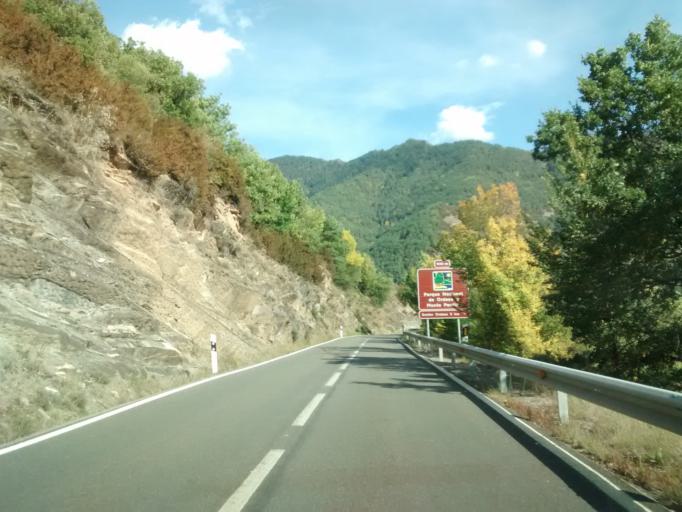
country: ES
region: Aragon
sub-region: Provincia de Huesca
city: Broto
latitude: 42.6130
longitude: -0.1229
